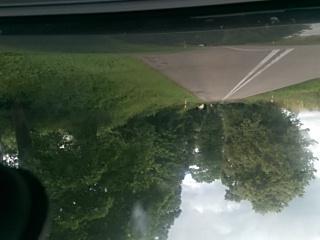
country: PL
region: Warmian-Masurian Voivodeship
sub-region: Powiat gizycki
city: Ryn
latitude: 54.0114
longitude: 21.5969
